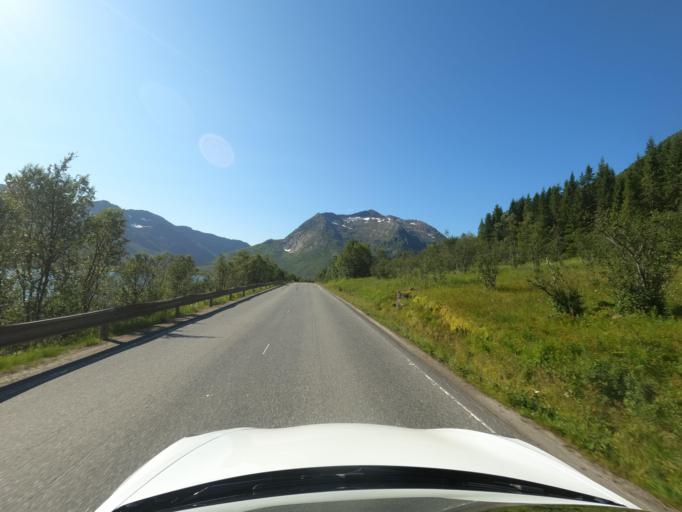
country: NO
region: Nordland
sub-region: Lodingen
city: Lodingen
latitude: 68.5493
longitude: 15.7459
